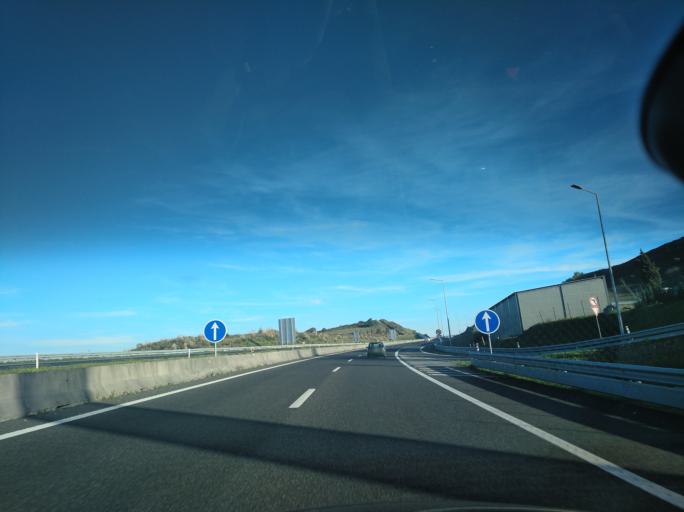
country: PT
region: Lisbon
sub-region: Sintra
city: Pero Pinheiro
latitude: 38.8179
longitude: -9.3256
